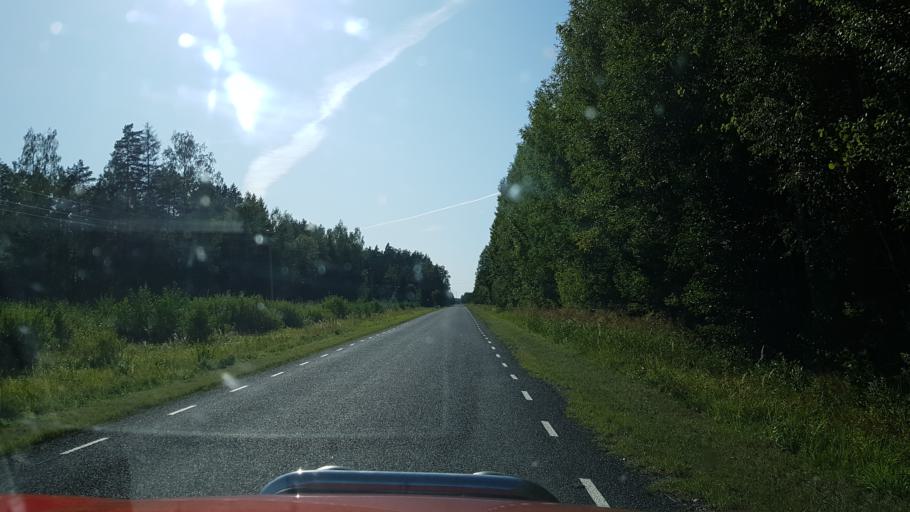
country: LV
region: Salacgrivas
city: Ainazi
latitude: 58.0819
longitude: 24.5636
